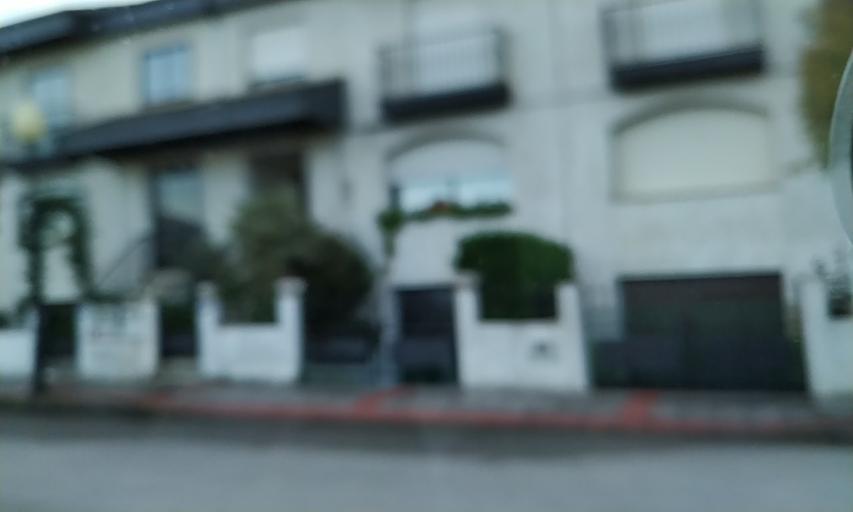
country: ES
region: Galicia
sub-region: Provincia de Ourense
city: Verin
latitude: 41.9214
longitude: -7.4438
